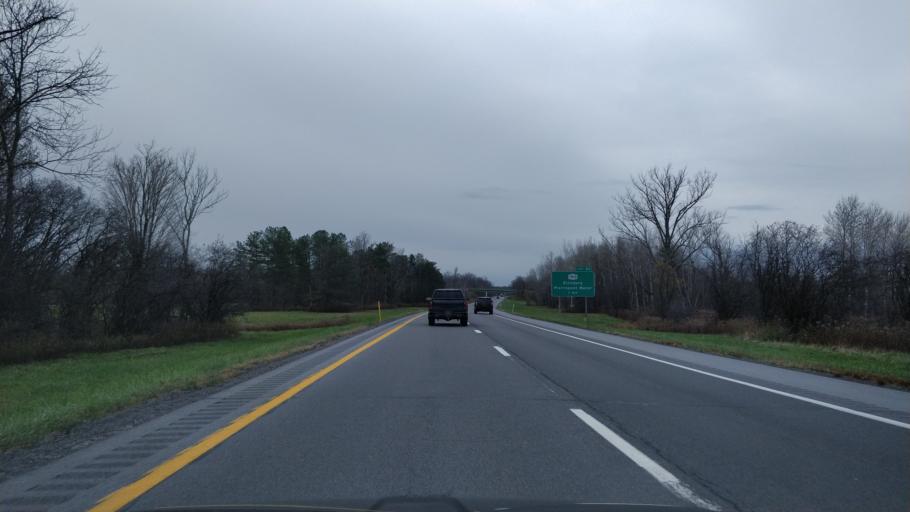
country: US
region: New York
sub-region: Jefferson County
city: Adams
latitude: 43.7524
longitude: -76.0617
